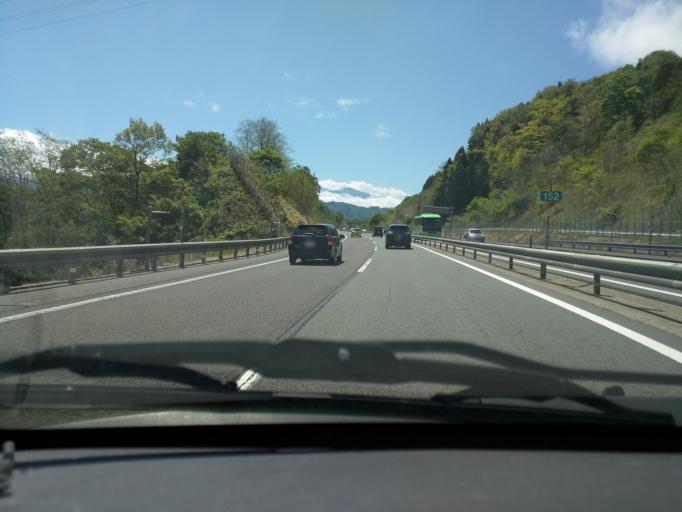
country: JP
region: Nagano
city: Nakano
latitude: 36.7797
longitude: 138.3173
